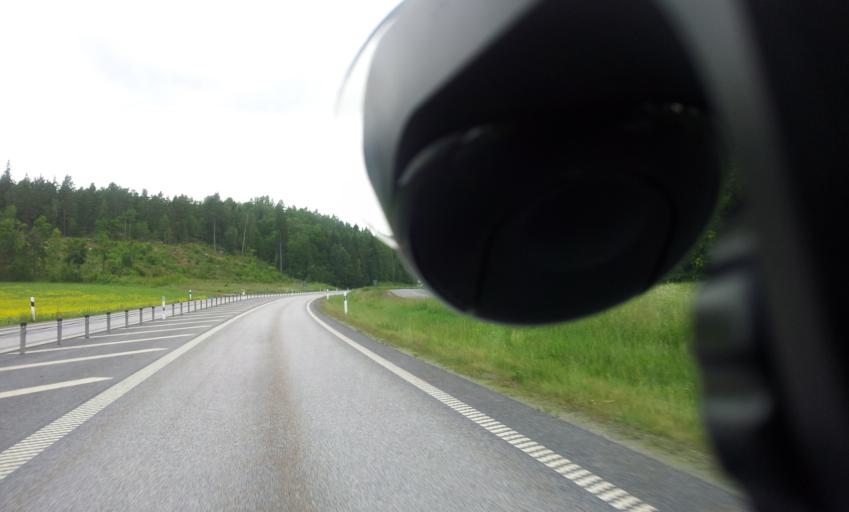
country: SE
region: Kalmar
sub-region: Vasterviks Kommun
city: Forserum
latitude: 57.9550
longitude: 16.4431
